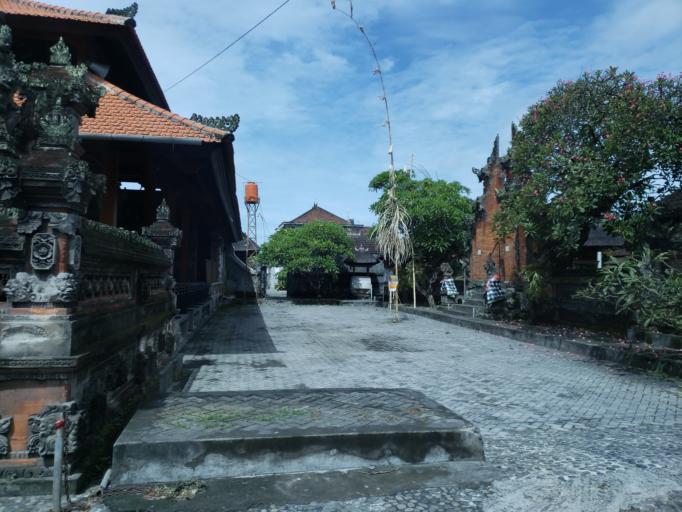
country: ID
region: Bali
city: Banjar Jabejero
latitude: -8.6048
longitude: 115.2528
